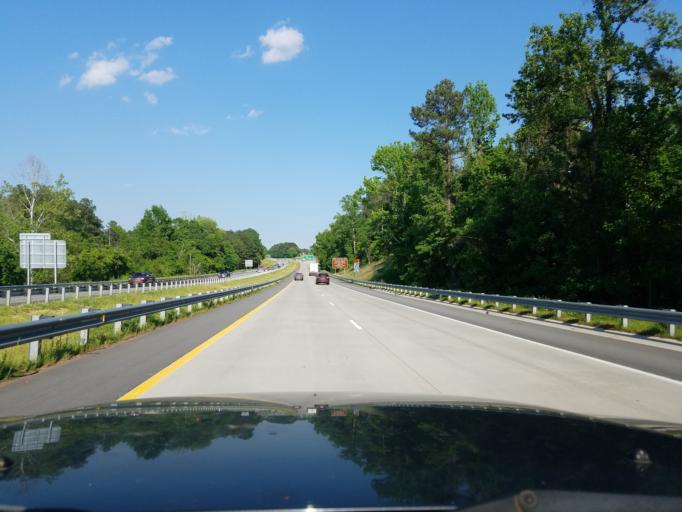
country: US
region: North Carolina
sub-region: Vance County
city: Henderson
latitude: 36.3393
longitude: -78.4212
